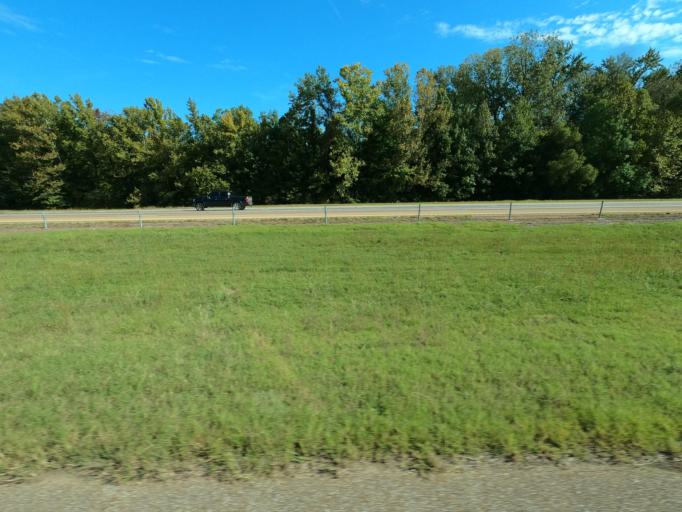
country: US
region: Tennessee
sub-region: Shelby County
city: Millington
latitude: 35.3167
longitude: -89.8694
